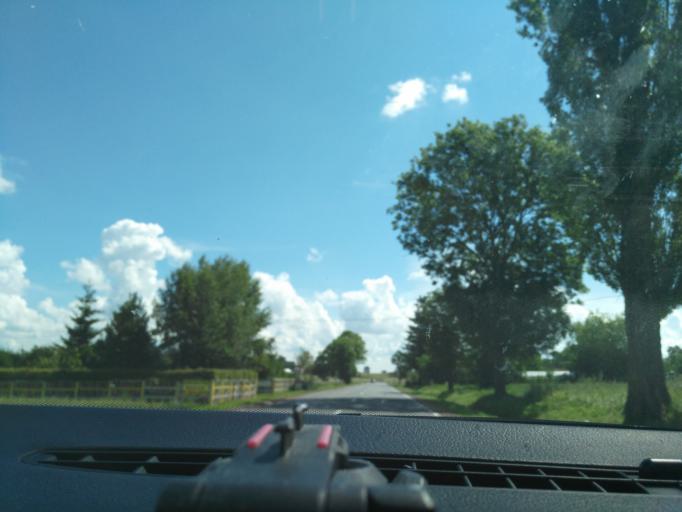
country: PL
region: Masovian Voivodeship
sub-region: Powiat losicki
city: Sarnaki
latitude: 52.2642
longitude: 22.8310
